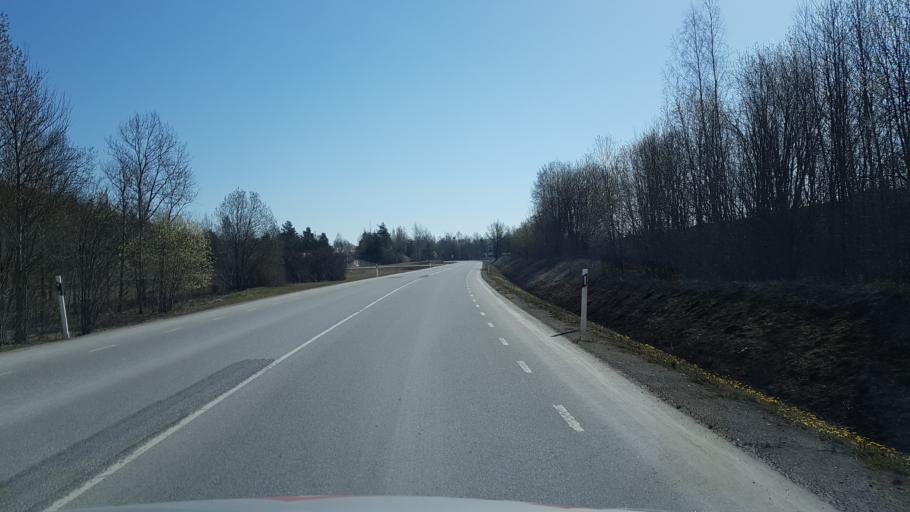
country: EE
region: Ida-Virumaa
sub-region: Kivioli linn
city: Kivioli
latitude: 59.3586
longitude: 26.9434
